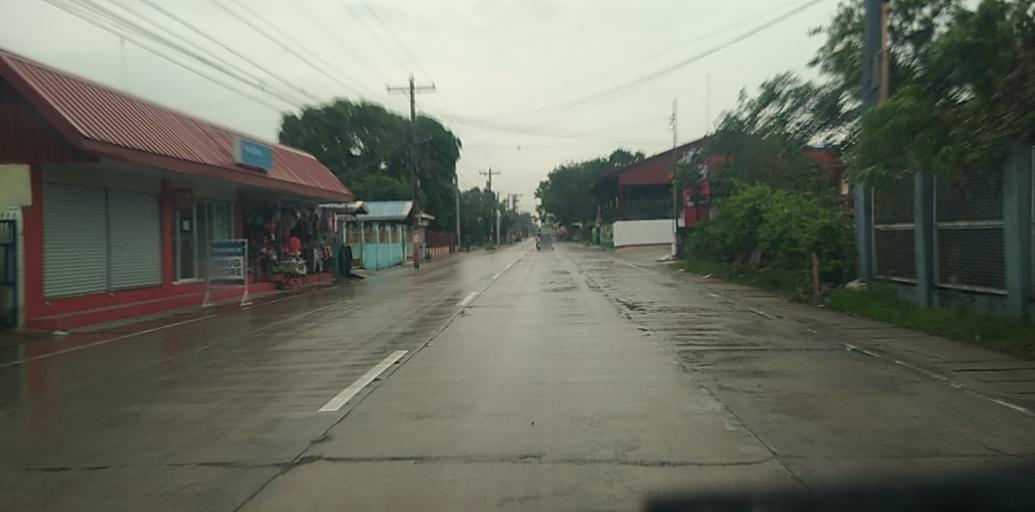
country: PH
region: Central Luzon
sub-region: Province of Pampanga
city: Anao
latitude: 15.1387
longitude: 120.6941
